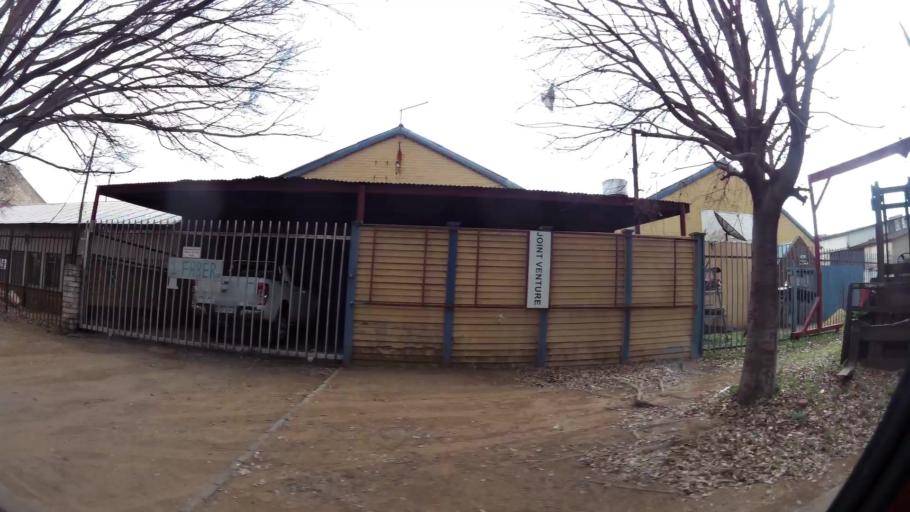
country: ZA
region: Gauteng
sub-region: Sedibeng District Municipality
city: Vanderbijlpark
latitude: -26.6898
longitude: 27.8095
